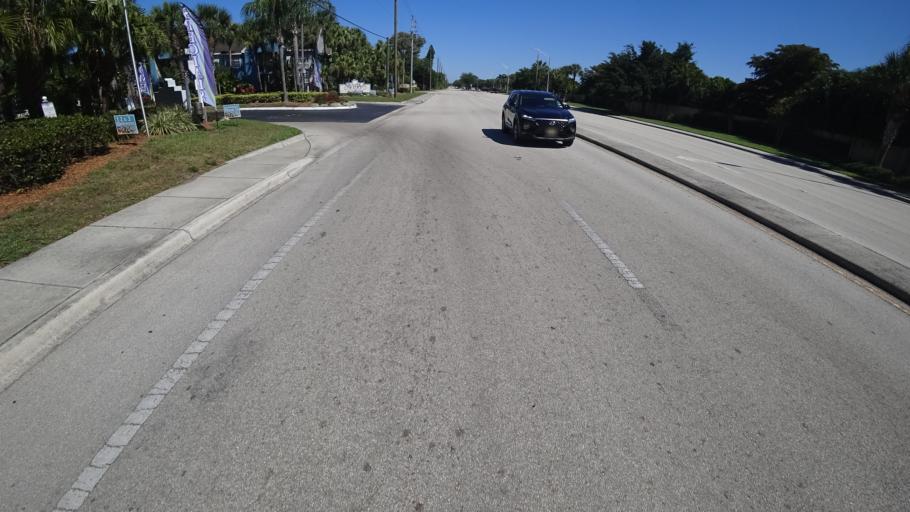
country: US
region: Florida
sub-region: Manatee County
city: West Bradenton
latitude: 27.4680
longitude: -82.6369
